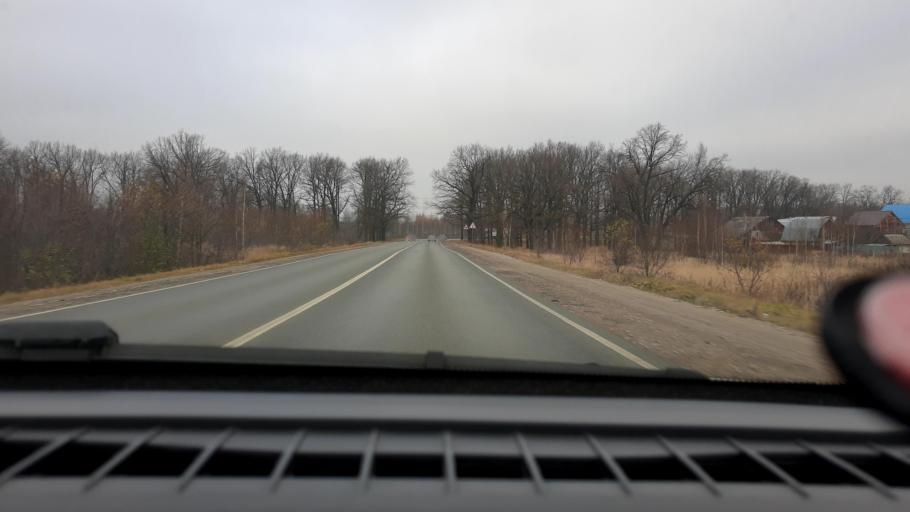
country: RU
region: Nizjnij Novgorod
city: Novaya Balakhna
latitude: 56.5121
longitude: 43.5793
